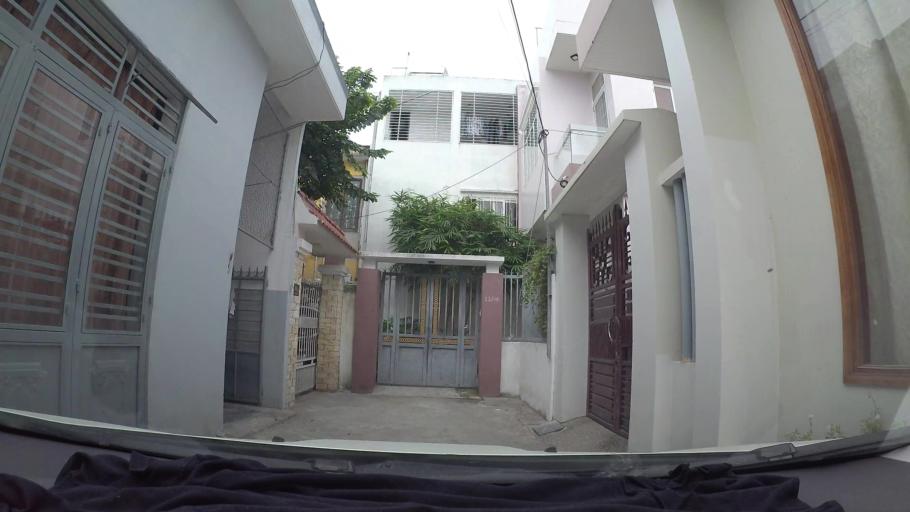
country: VN
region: Da Nang
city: Thanh Khe
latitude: 16.0703
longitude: 108.1896
